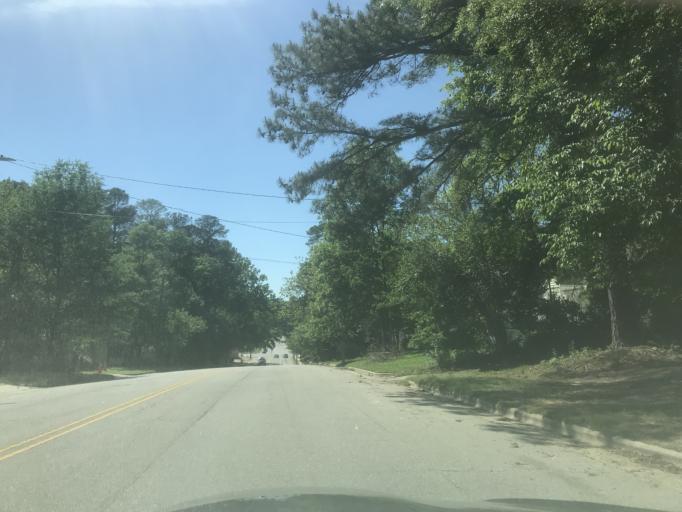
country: US
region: North Carolina
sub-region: Wake County
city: Raleigh
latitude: 35.7486
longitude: -78.6462
